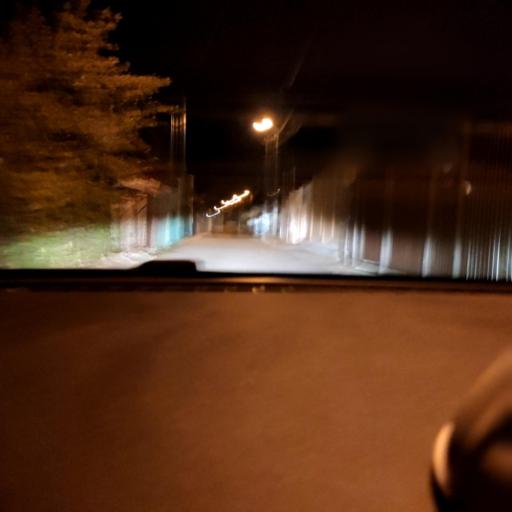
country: RU
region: Samara
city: Samara
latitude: 53.2525
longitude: 50.1927
